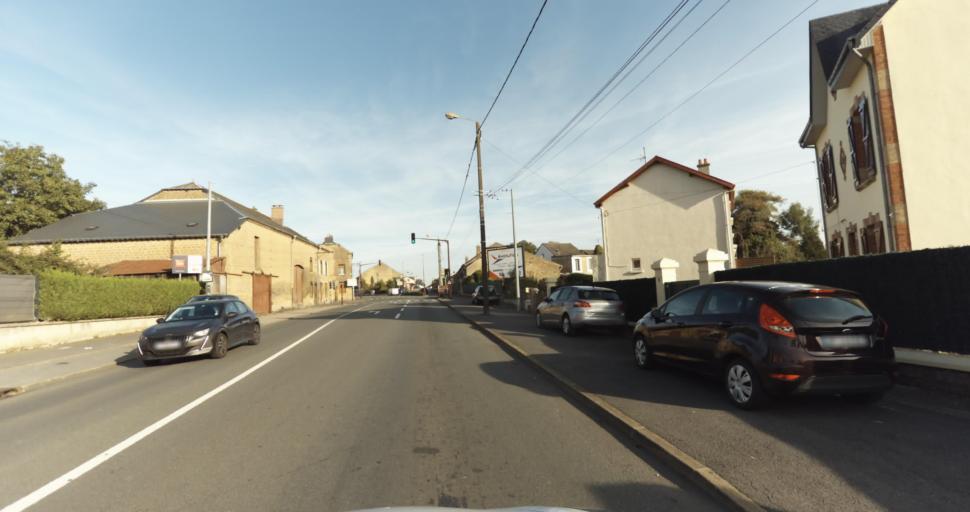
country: FR
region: Champagne-Ardenne
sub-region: Departement des Ardennes
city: Villers-Semeuse
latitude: 49.7385
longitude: 4.7483
